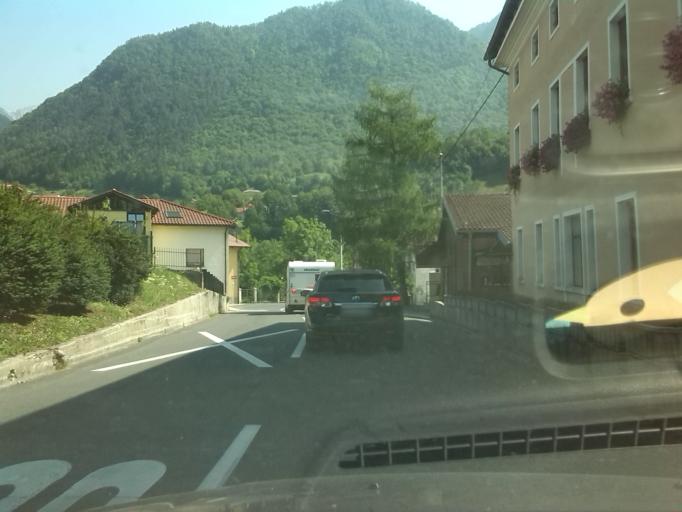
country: SI
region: Tolmin
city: Tolmin
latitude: 46.1844
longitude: 13.7376
